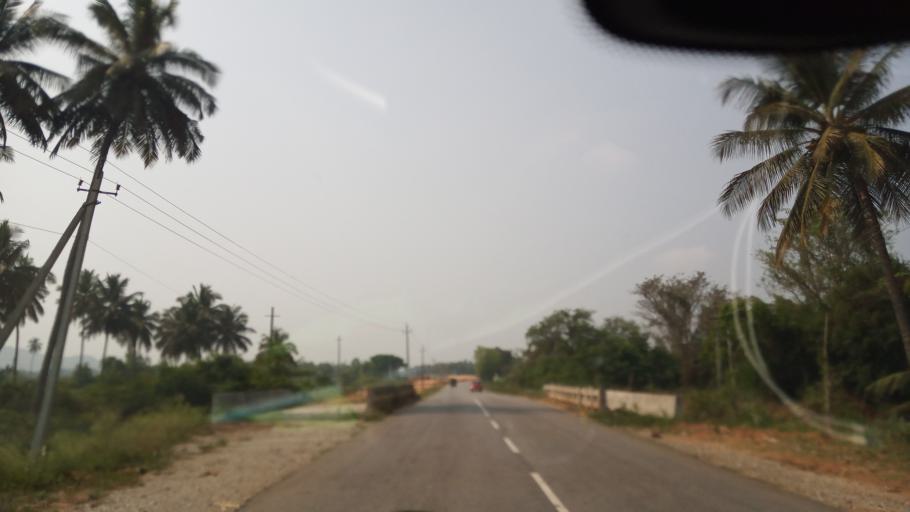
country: IN
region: Karnataka
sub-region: Mandya
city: Pandavapura
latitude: 12.5278
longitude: 76.6717
